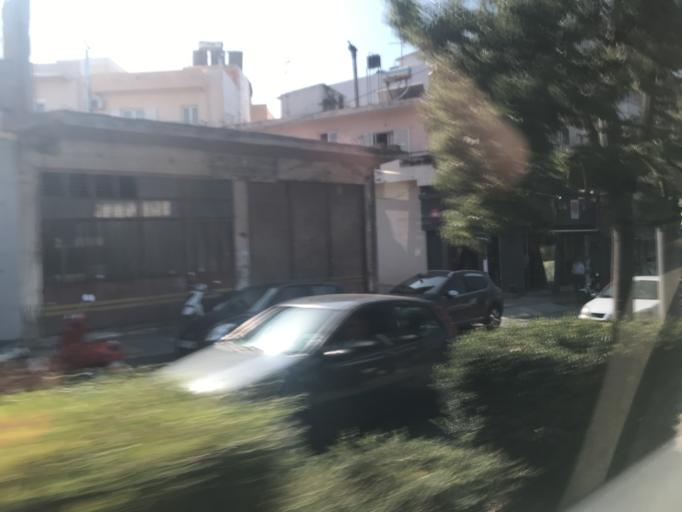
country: GR
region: Crete
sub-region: Nomos Irakleiou
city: Irakleion
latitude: 35.3334
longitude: 25.1149
